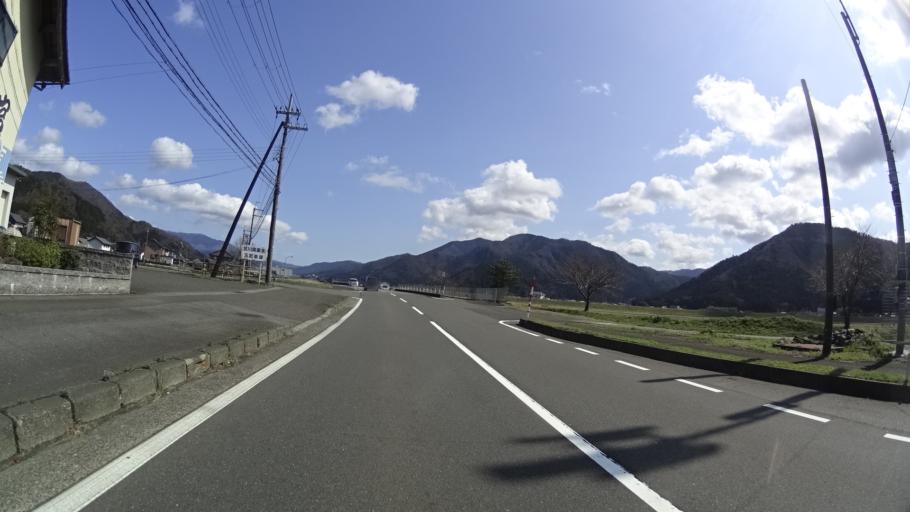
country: JP
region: Fukui
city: Obama
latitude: 35.4783
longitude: 135.8165
